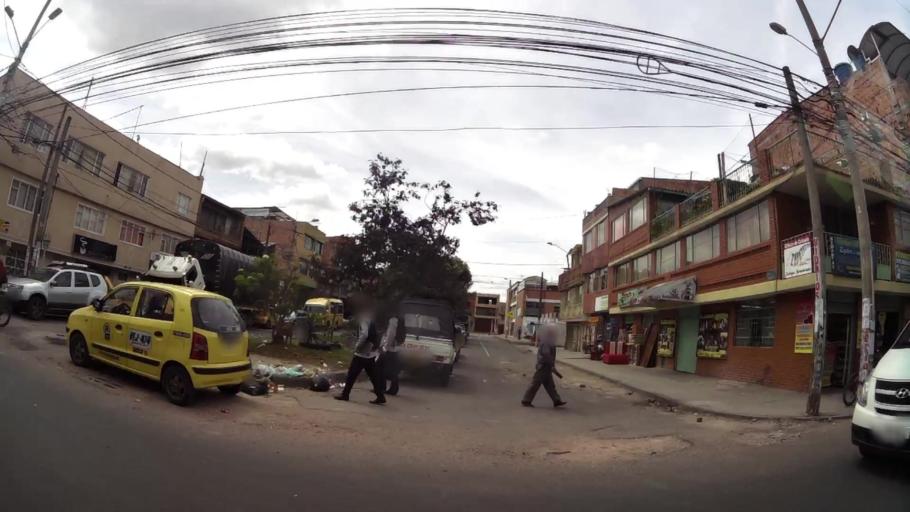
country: CO
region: Cundinamarca
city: Soacha
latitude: 4.6400
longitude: -74.1598
